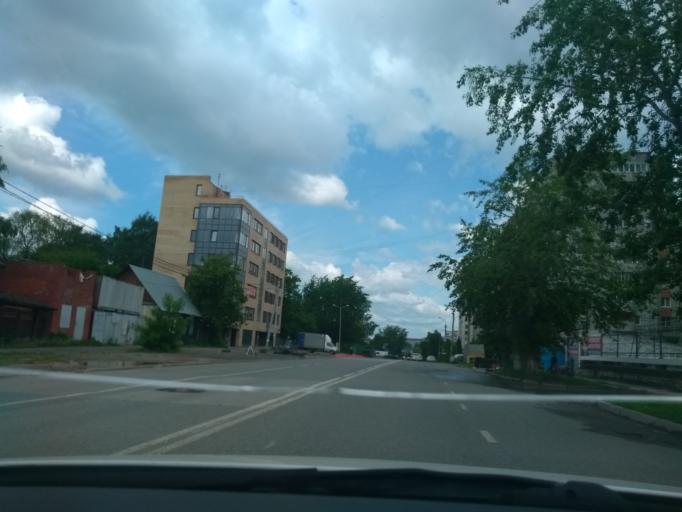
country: RU
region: Perm
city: Perm
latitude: 58.0016
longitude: 56.2161
